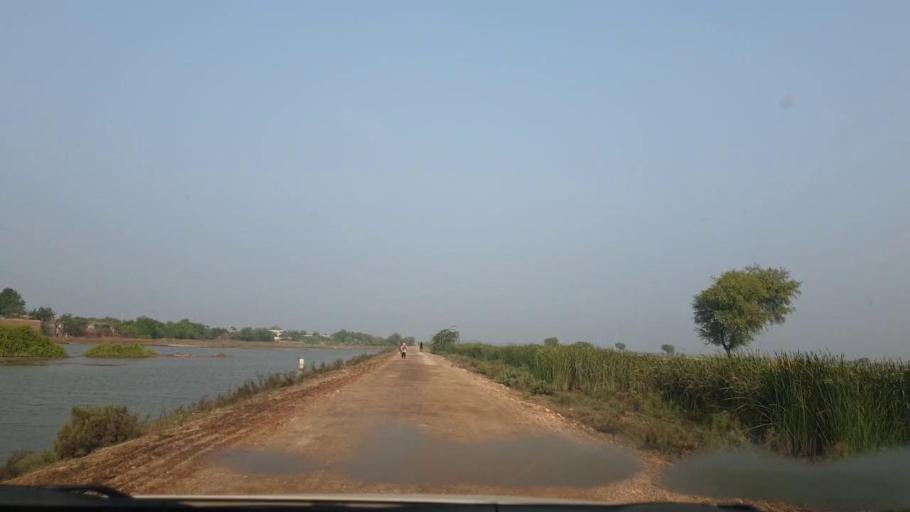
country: PK
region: Sindh
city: Tando Muhammad Khan
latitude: 25.0898
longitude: 68.4812
